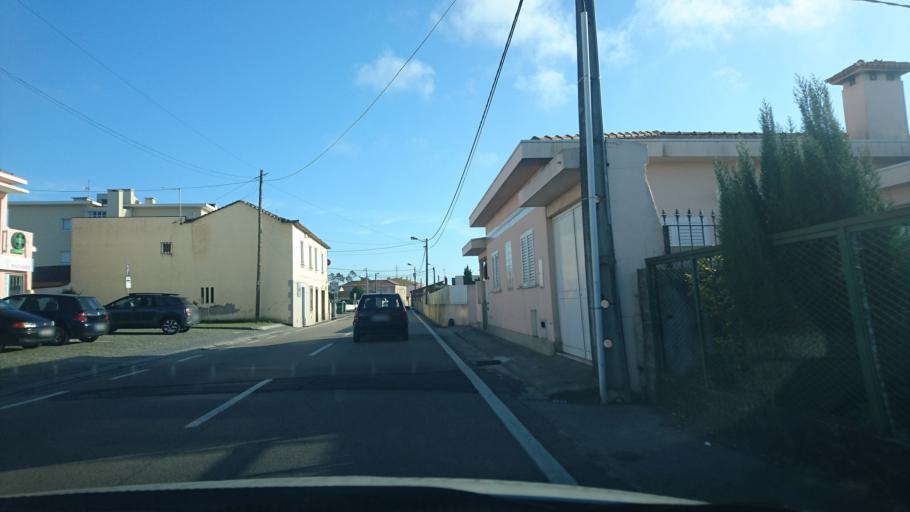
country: PT
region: Aveiro
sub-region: Espinho
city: Souto
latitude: 40.9735
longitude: -8.6303
